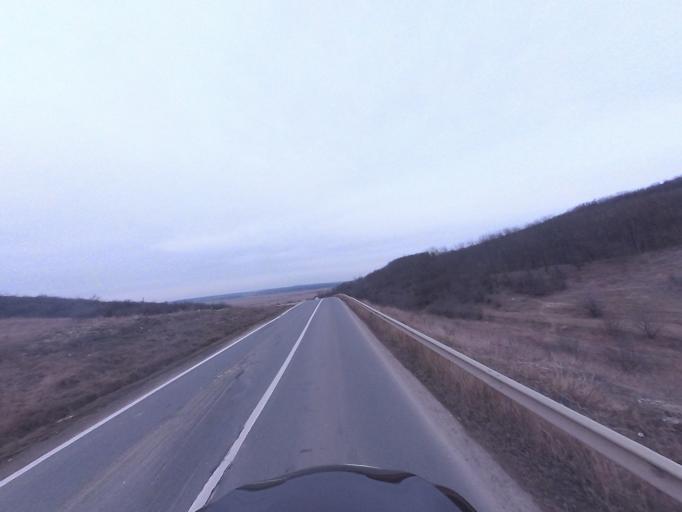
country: RO
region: Iasi
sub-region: Comuna Popricani
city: Popricani
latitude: 47.2977
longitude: 27.5100
